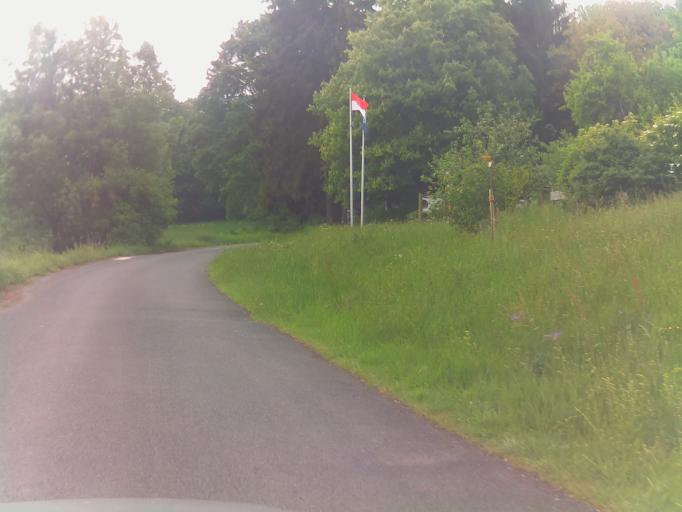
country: DE
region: Bavaria
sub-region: Regierungsbezirk Unterfranken
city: Oberelsbach
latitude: 50.4654
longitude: 10.0954
